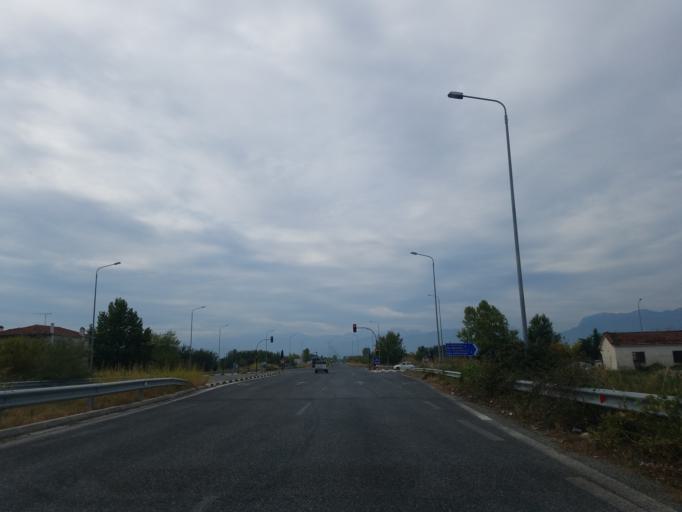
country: GR
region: Thessaly
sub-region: Trikala
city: Pyrgetos
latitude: 39.5676
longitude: 21.7397
